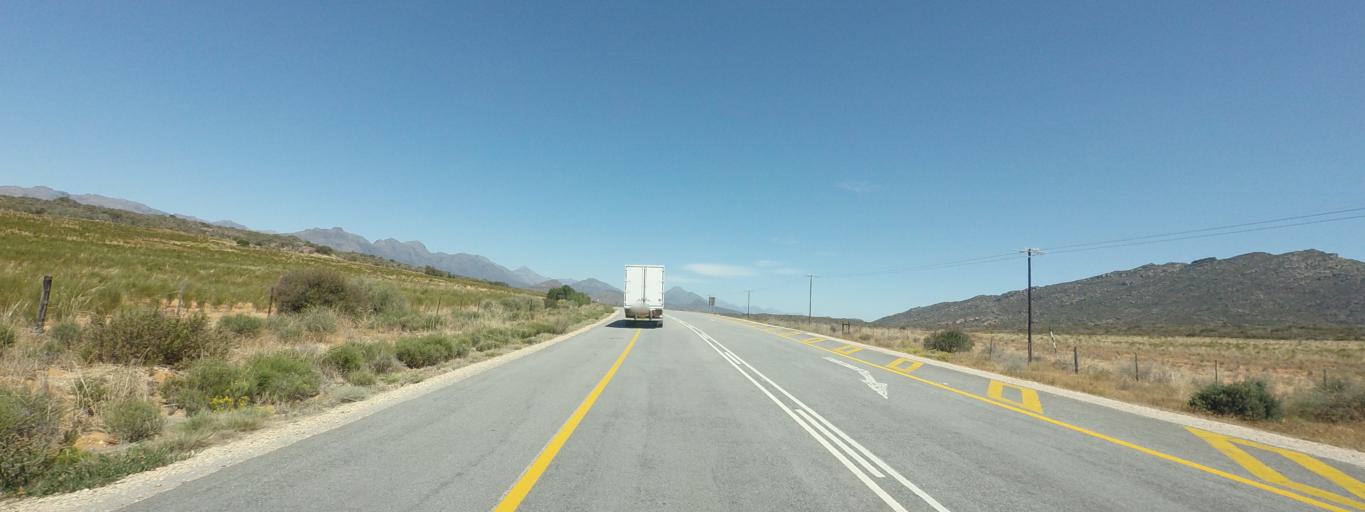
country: ZA
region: Western Cape
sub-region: West Coast District Municipality
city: Clanwilliam
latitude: -32.3191
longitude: 18.9134
